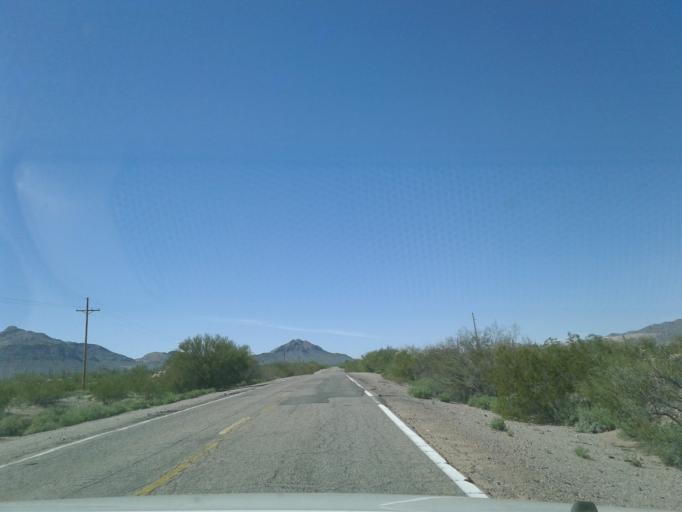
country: US
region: Arizona
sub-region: Pima County
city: Avra Valley
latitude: 32.3711
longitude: -111.4214
